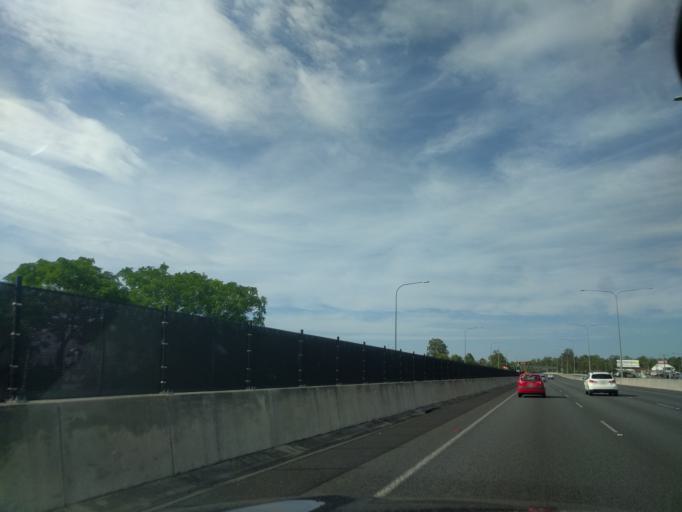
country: AU
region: Queensland
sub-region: Brisbane
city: Wacol
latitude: -27.5901
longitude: 152.9260
